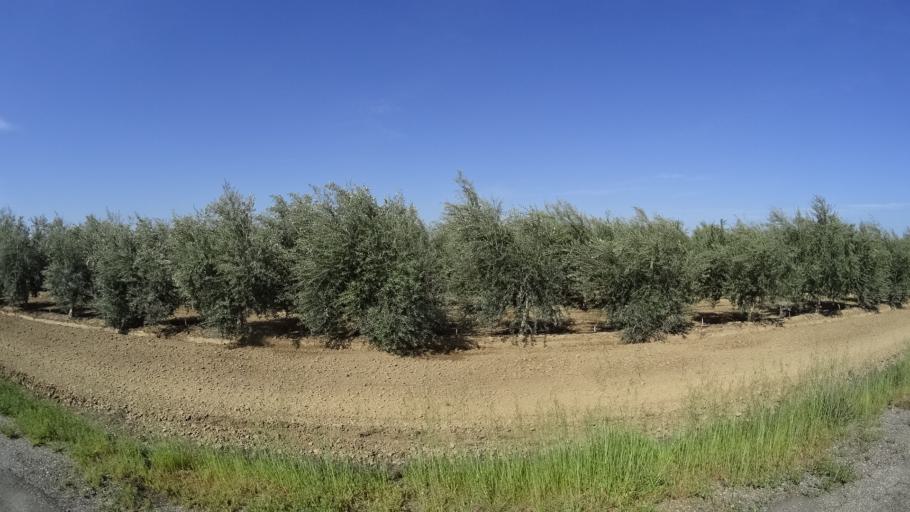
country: US
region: California
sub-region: Glenn County
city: Hamilton City
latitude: 39.6657
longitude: -122.0180
